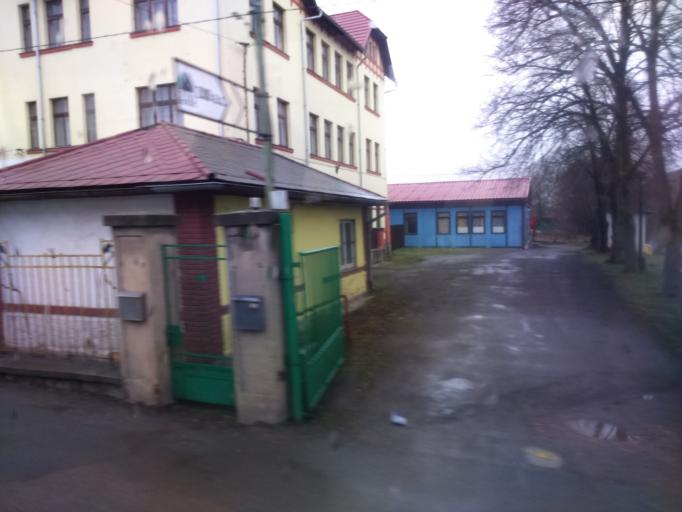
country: CZ
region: Plzensky
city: Zbuch
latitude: 49.6838
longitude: 13.2344
